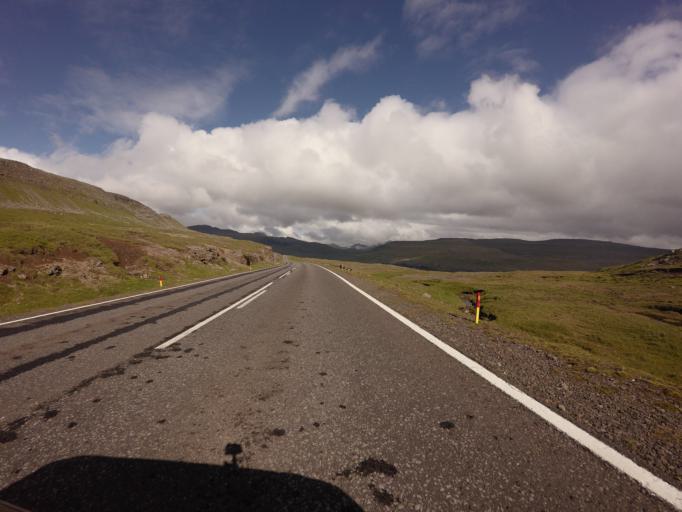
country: FO
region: Streymoy
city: Kollafjordhur
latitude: 62.0442
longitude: -6.8873
